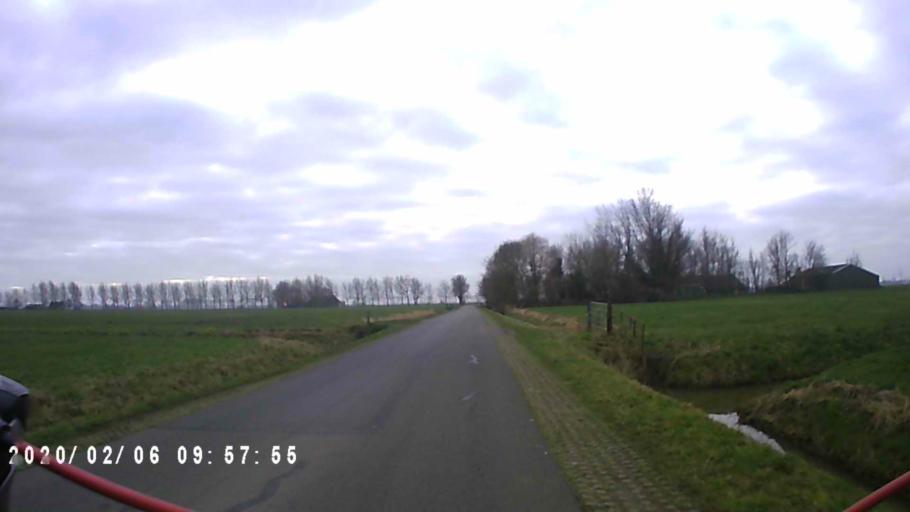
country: NL
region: Groningen
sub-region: Gemeente Zuidhorn
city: Aduard
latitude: 53.2730
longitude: 6.4965
